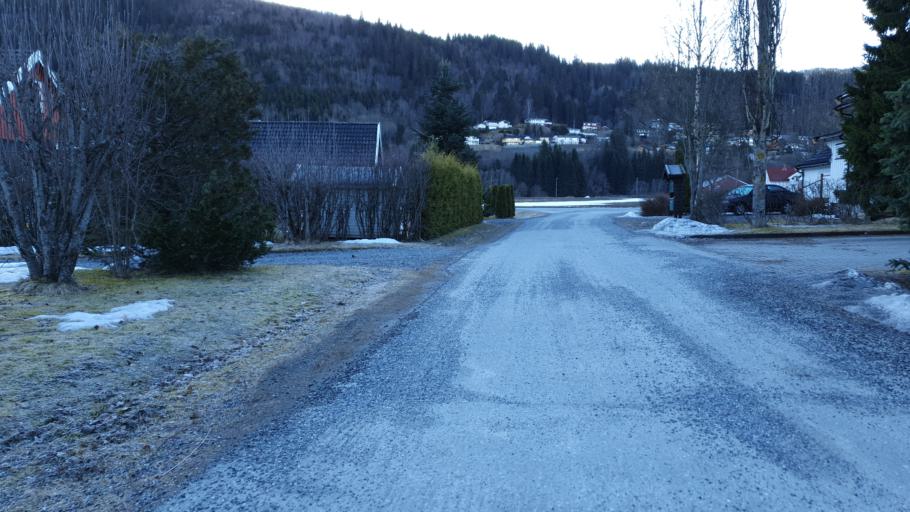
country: NO
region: Sor-Trondelag
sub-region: Orkdal
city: Orkanger
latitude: 63.2903
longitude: 9.8456
